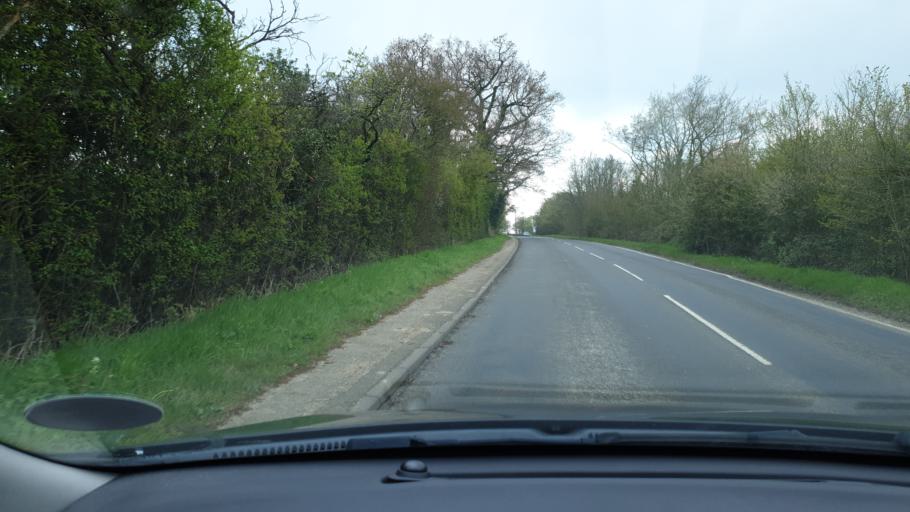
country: GB
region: England
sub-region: Essex
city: Alresford
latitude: 51.8913
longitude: 1.0283
